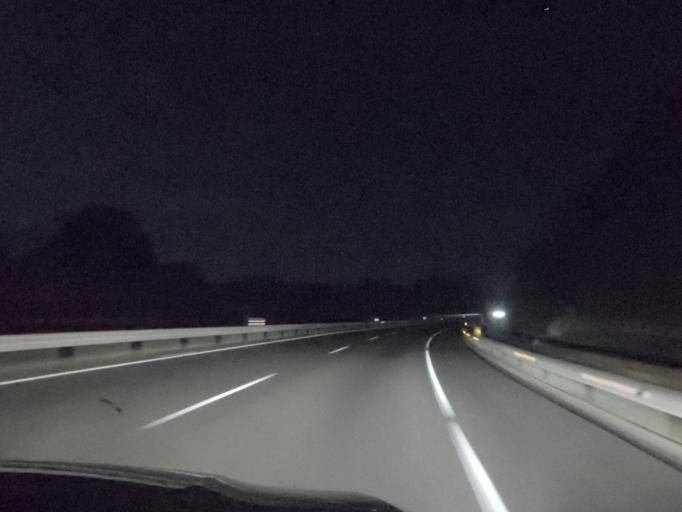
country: ES
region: Galicia
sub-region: Provincia de Ourense
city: Taboadela
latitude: 42.2343
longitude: -7.8484
